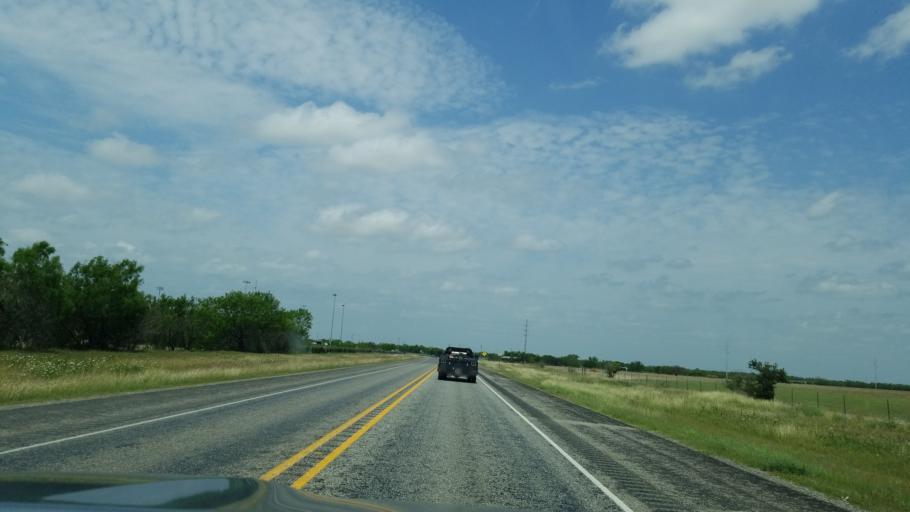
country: US
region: Texas
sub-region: Zavala County
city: La Pryor
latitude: 28.9435
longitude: -99.8294
